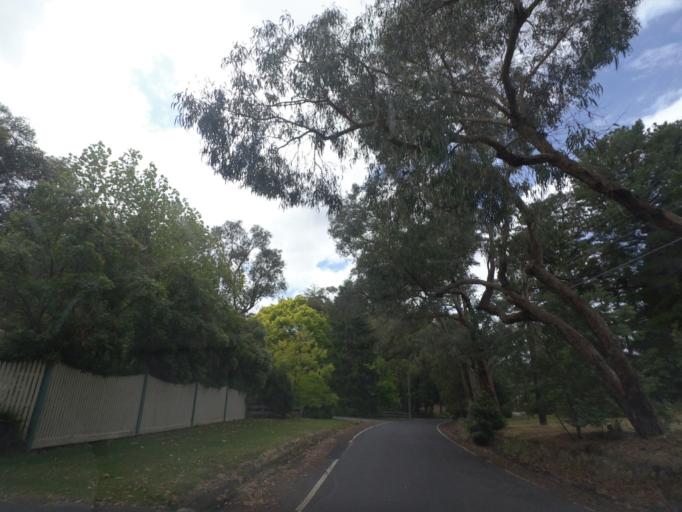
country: AU
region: Victoria
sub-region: Manningham
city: Park Orchards
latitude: -37.7964
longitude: 145.2079
